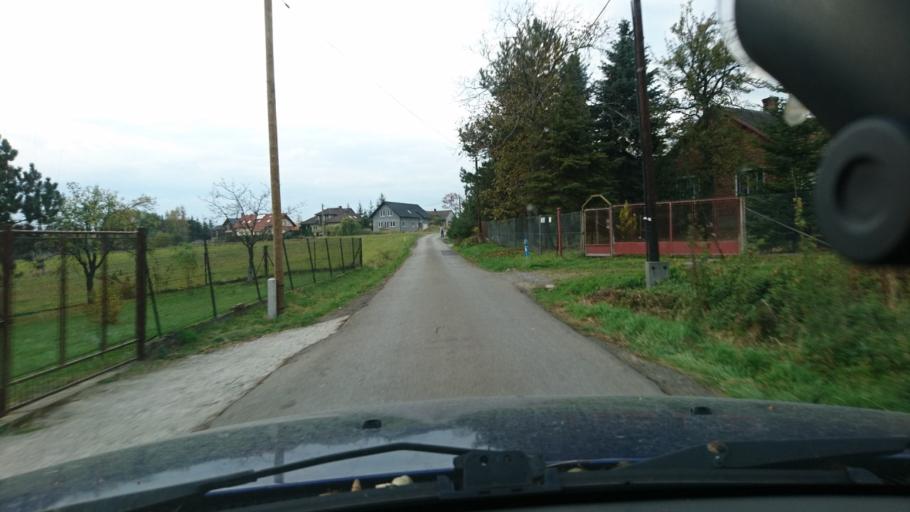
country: PL
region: Silesian Voivodeship
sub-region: Powiat bielski
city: Kozy
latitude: 49.8636
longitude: 19.1591
